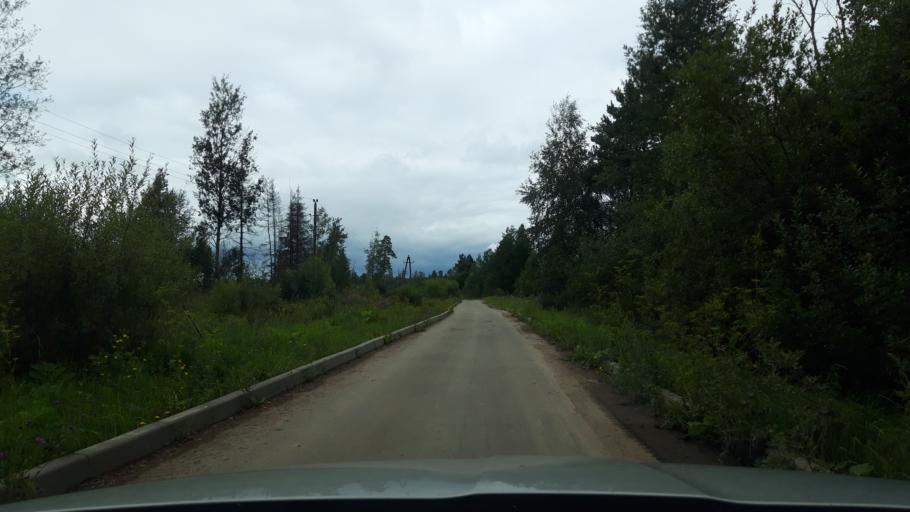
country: RU
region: Moskovskaya
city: Povarovo
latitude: 56.0431
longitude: 37.0546
